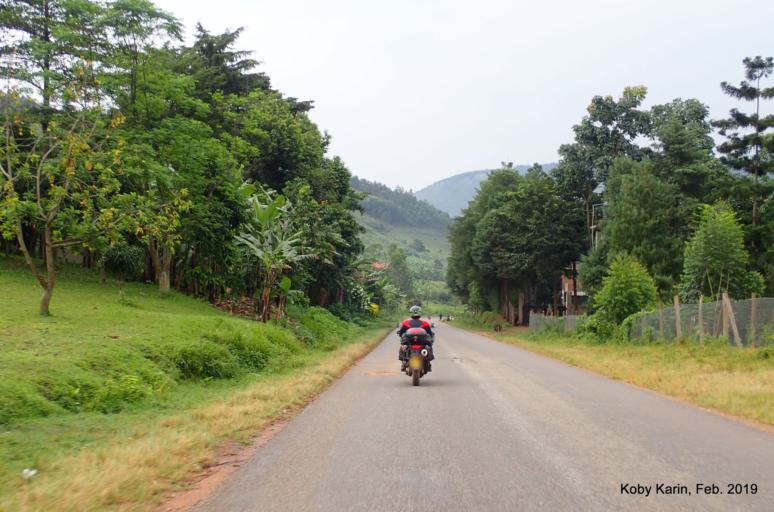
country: UG
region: Western Region
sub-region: Rubirizi District
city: Rubirizi
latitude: -0.3274
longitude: 30.1059
